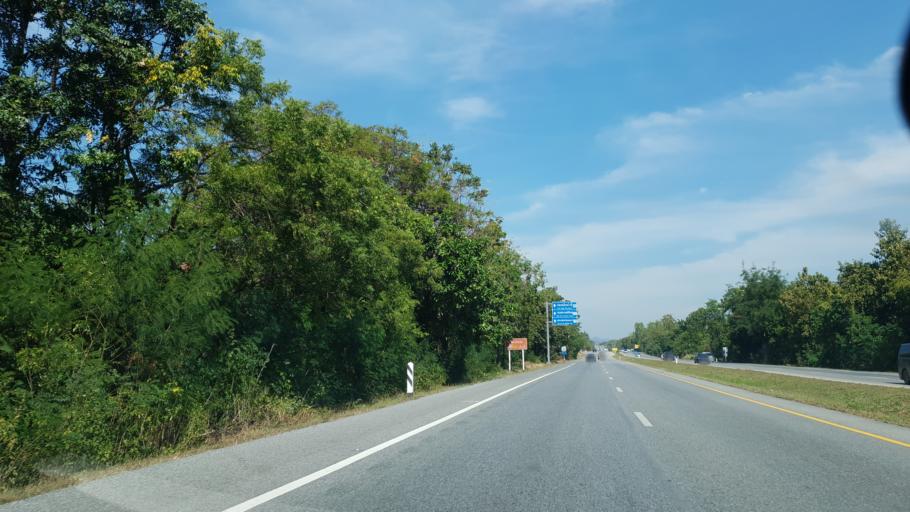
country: TH
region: Uttaradit
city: Thong Saen Khan
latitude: 17.4295
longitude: 100.2267
